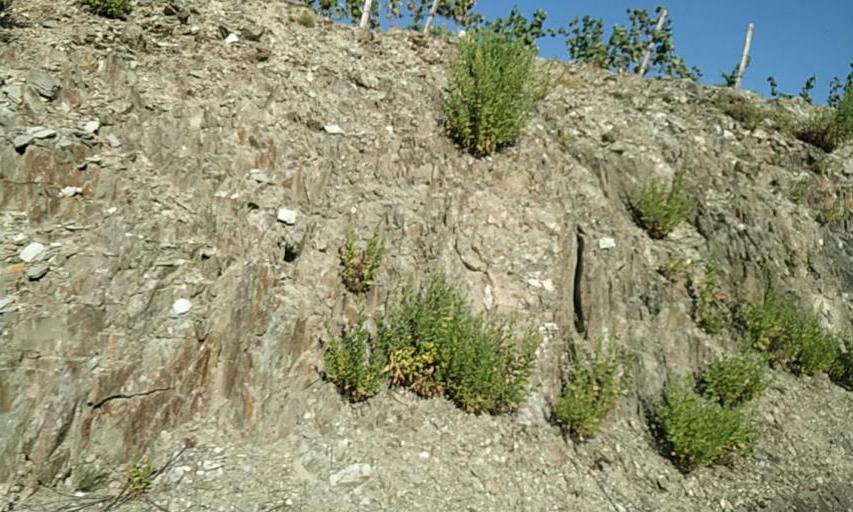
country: PT
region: Viseu
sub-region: Sao Joao da Pesqueira
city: Sao Joao da Pesqueira
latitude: 41.1759
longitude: -7.4368
